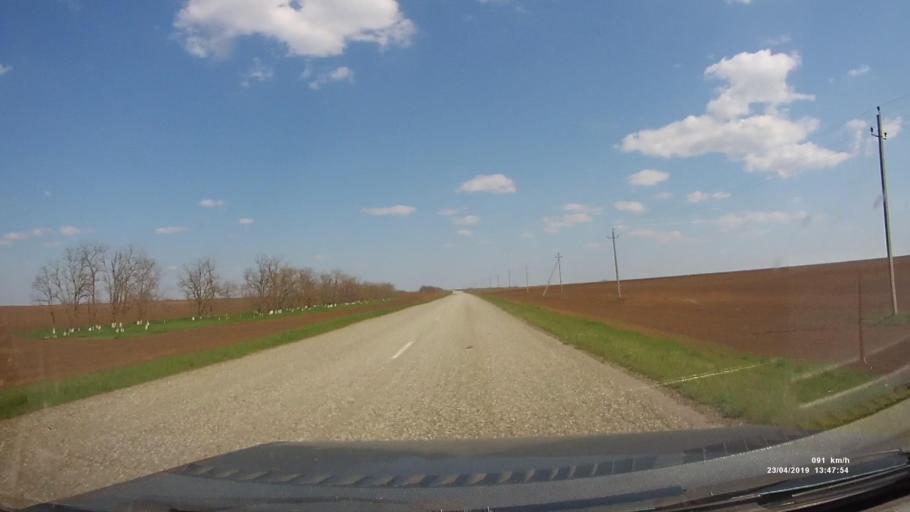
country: RU
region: Kalmykiya
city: Yashalta
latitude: 46.5991
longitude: 42.8645
